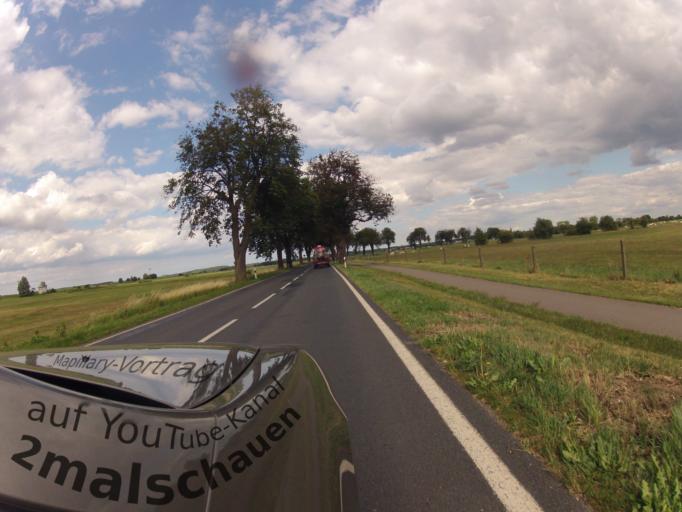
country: DE
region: Mecklenburg-Vorpommern
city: Usedom
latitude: 53.8741
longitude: 13.8916
